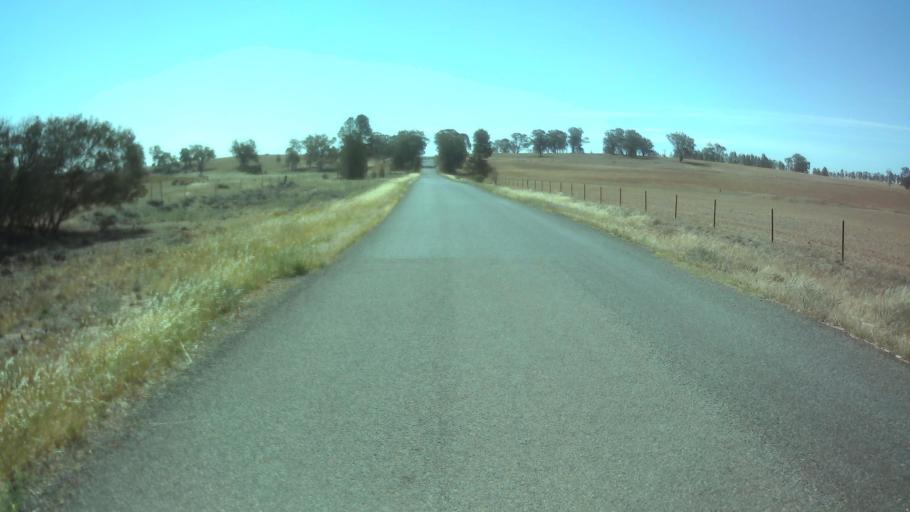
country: AU
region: New South Wales
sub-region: Weddin
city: Grenfell
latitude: -33.7604
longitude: 147.8601
